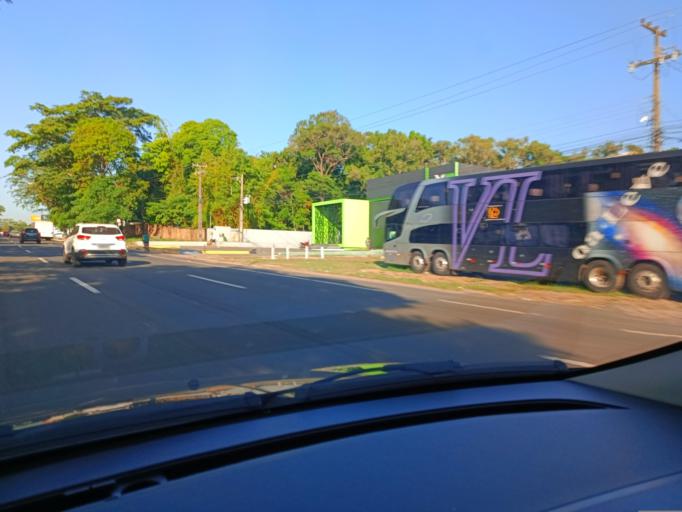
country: BR
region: Piaui
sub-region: Teresina
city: Teresina
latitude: -5.0803
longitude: -42.7571
